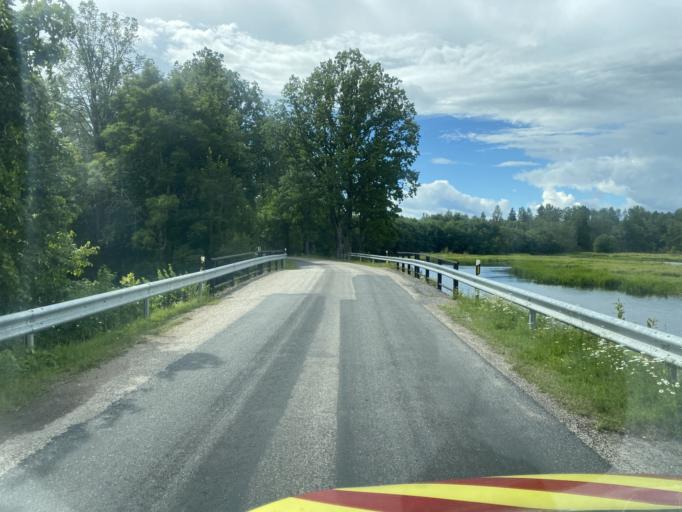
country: EE
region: Valgamaa
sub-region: Torva linn
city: Torva
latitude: 57.9463
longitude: 25.8809
